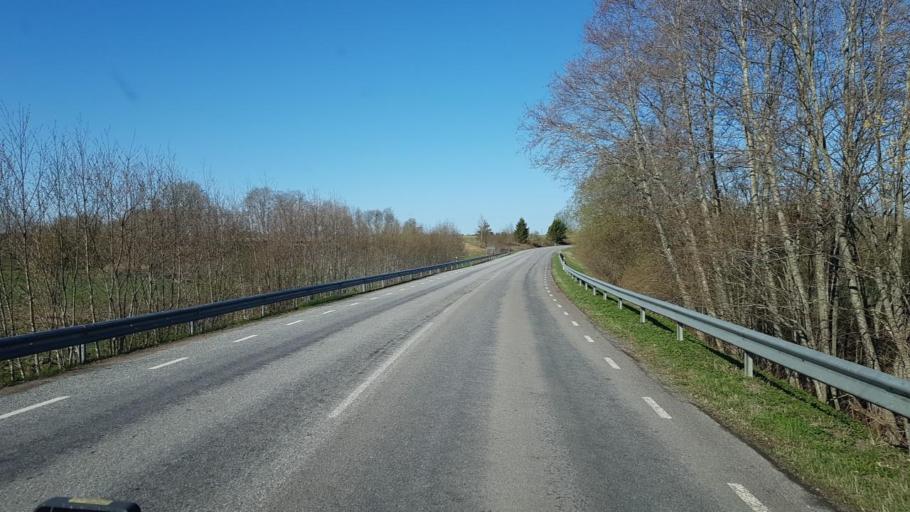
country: EE
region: Laeaene-Virumaa
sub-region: Vinni vald
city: Vinni
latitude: 59.3178
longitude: 26.4859
